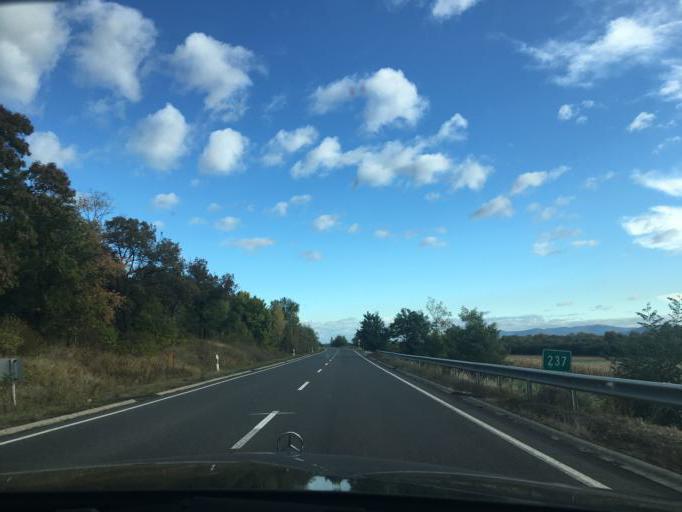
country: HU
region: Borsod-Abauj-Zemplen
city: Gonc
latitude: 48.4554
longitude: 21.1919
